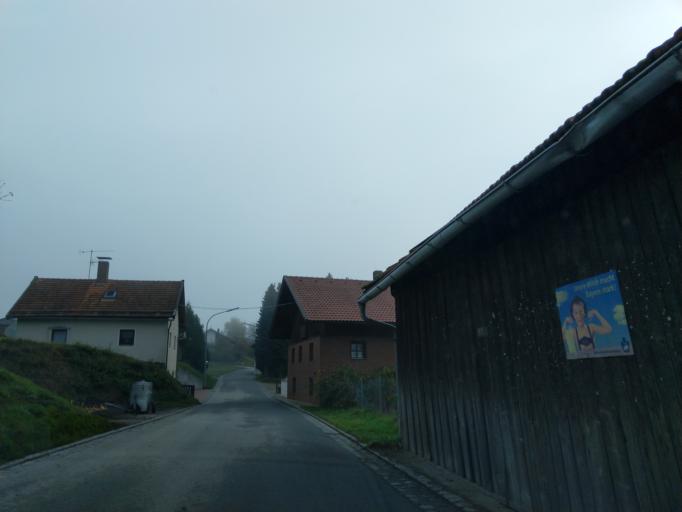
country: DE
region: Bavaria
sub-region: Lower Bavaria
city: Grattersdorf
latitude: 48.7950
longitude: 13.1548
